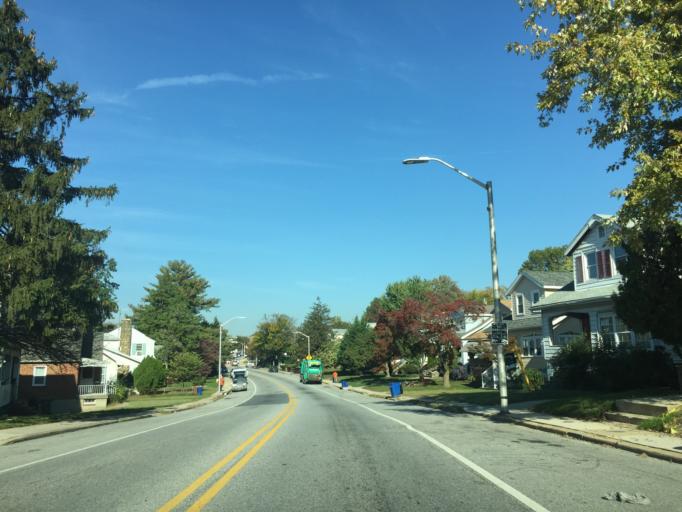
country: US
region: Maryland
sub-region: Baltimore County
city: Parkville
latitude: 39.3481
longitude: -76.5606
